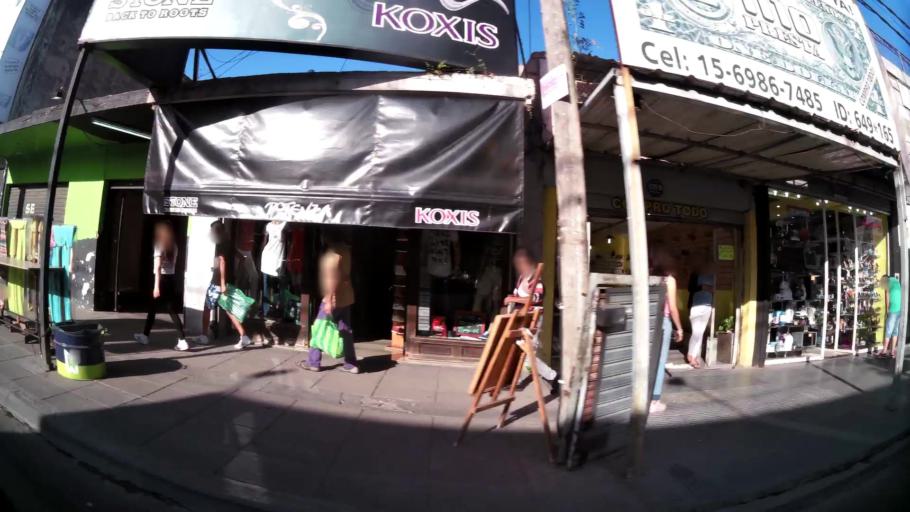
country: AR
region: Buenos Aires
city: Santa Catalina - Dique Lujan
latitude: -34.4868
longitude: -58.7261
